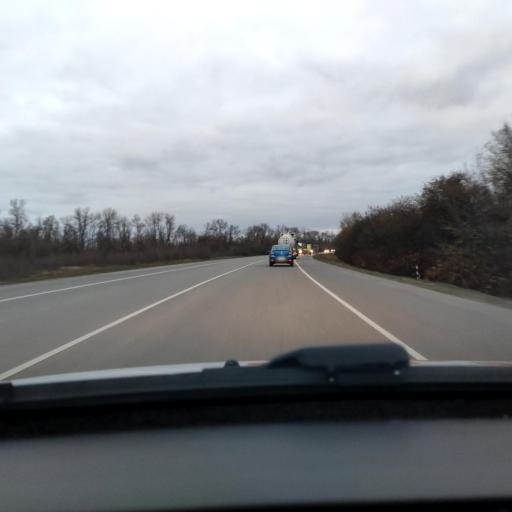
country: RU
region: Lipetsk
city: Borinskoye
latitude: 52.4542
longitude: 39.3002
